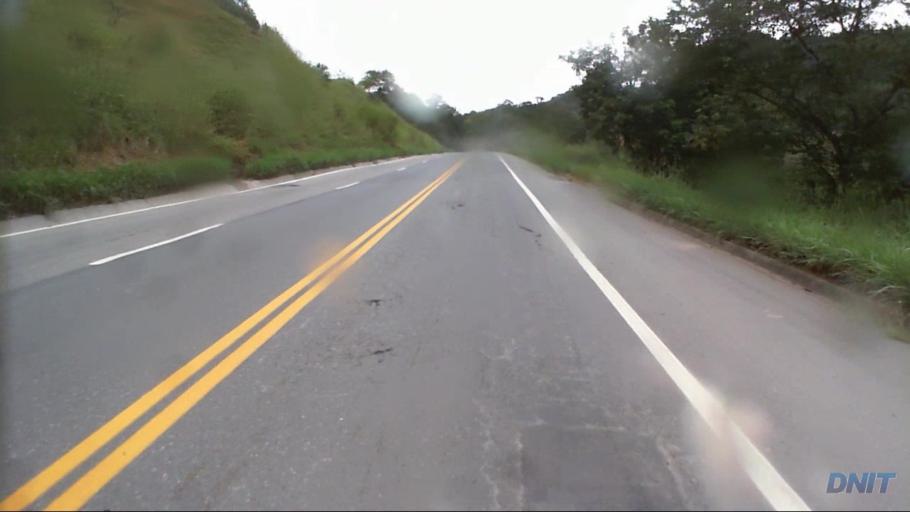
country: BR
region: Minas Gerais
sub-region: Nova Era
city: Nova Era
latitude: -19.7071
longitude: -42.9994
